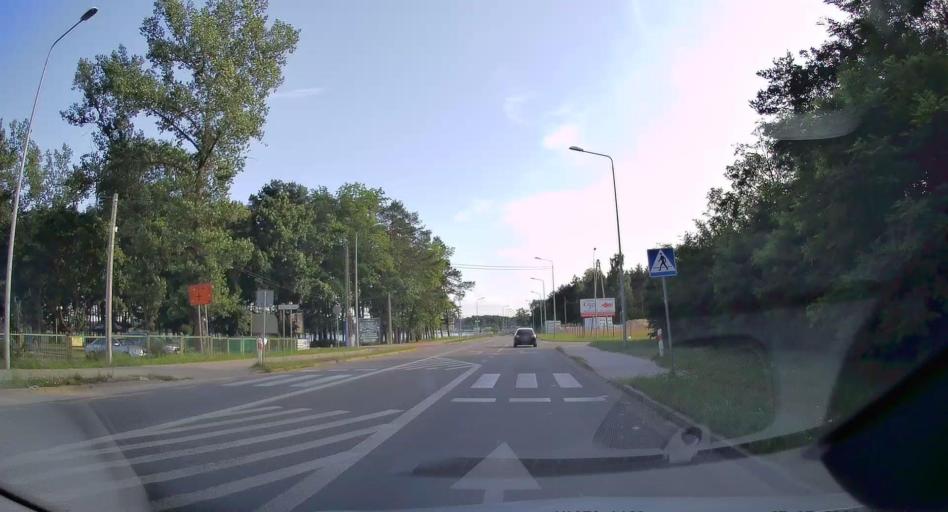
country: PL
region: Swietokrzyskie
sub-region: Powiat konecki
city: Smykow
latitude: 51.1191
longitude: 20.3524
